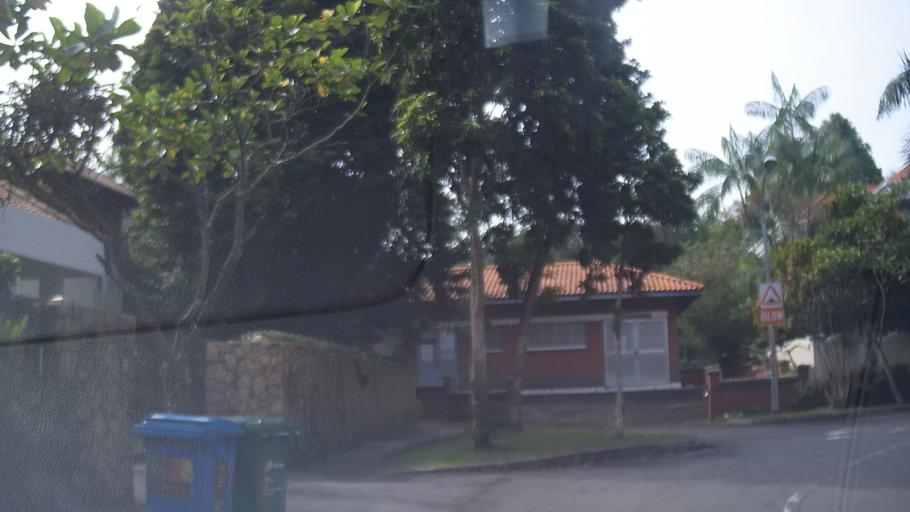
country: MY
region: Johor
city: Johor Bahru
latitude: 1.4272
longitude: 103.7801
